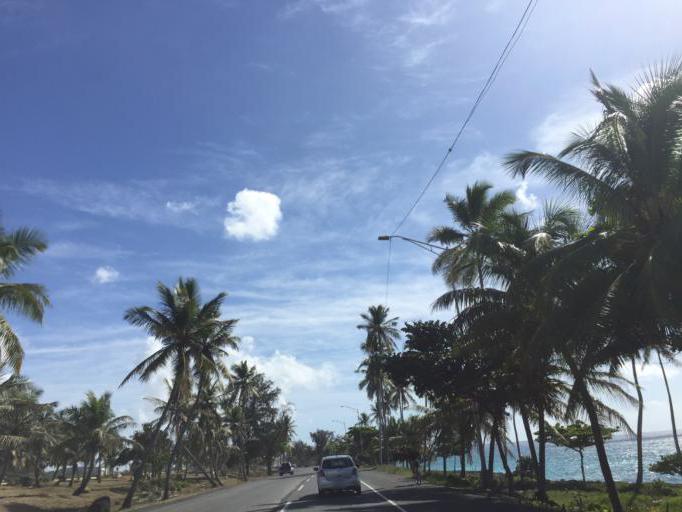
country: DO
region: Santo Domingo
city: Guerra
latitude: 18.4606
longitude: -69.7303
